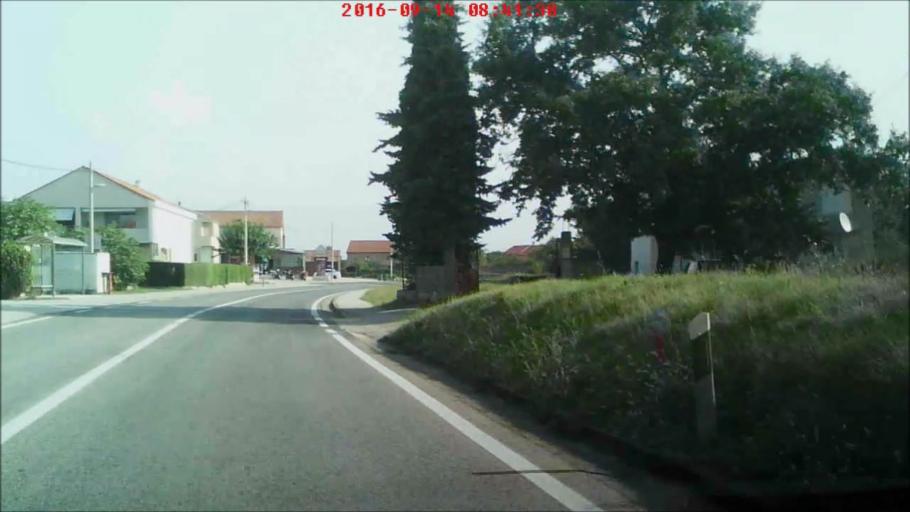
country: HR
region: Zadarska
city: Policnik
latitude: 44.1873
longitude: 15.3973
